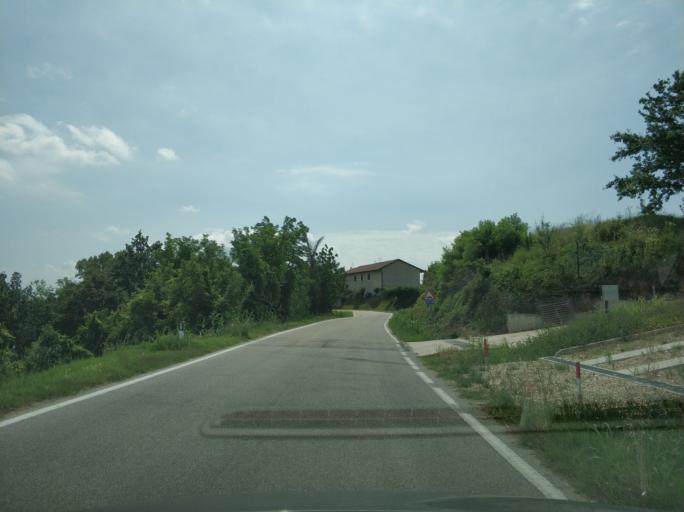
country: IT
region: Piedmont
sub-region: Provincia di Cuneo
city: Santo Stefano Roero
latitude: 44.7847
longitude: 7.9469
